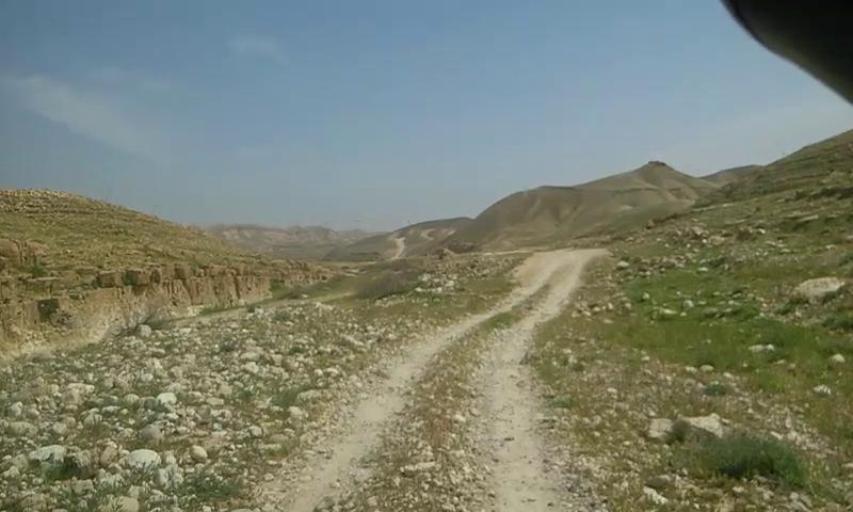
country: PS
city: `Arab ar Rashaydah
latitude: 31.5071
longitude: 35.2848
